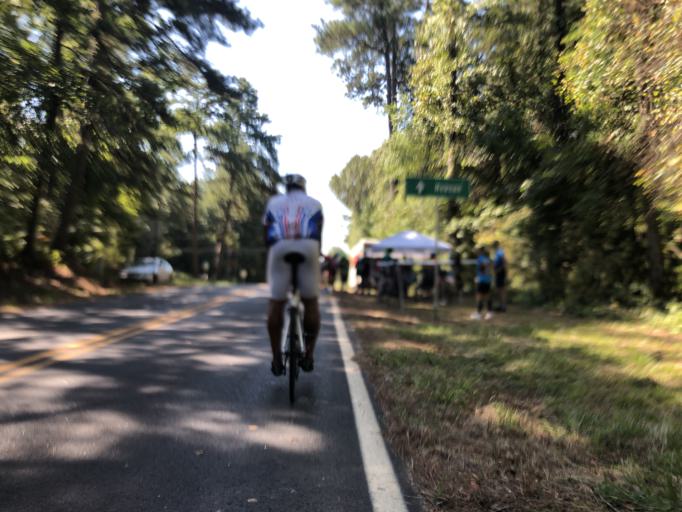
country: US
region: Georgia
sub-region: Heard County
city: Franklin
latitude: 33.3776
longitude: -84.9691
